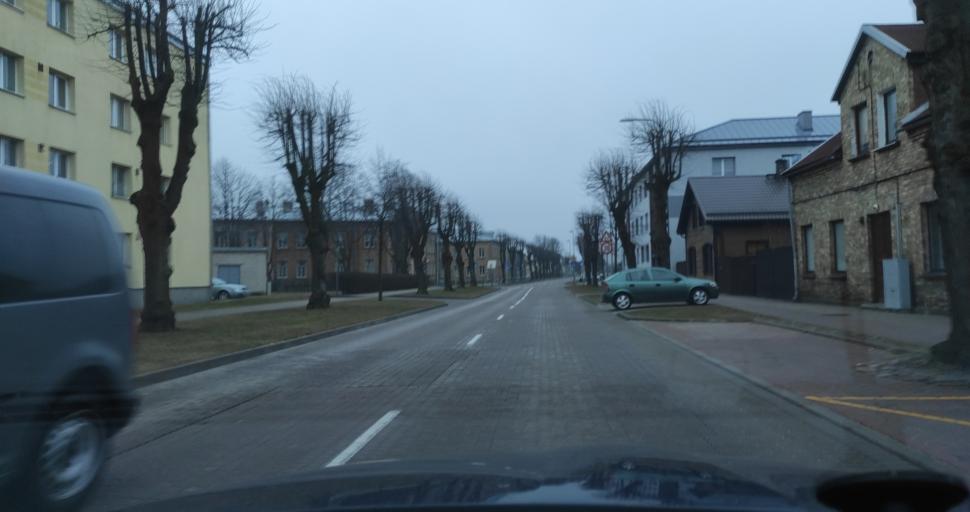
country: LV
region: Ventspils
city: Ventspils
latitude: 57.3891
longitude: 21.5585
